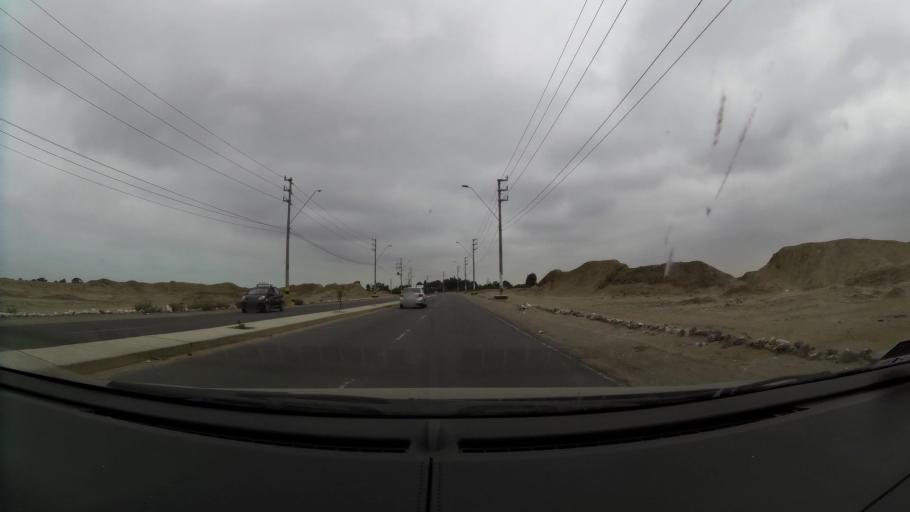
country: PE
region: La Libertad
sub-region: Provincia de Trujillo
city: La Esperanza
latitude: -8.0963
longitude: -79.0703
